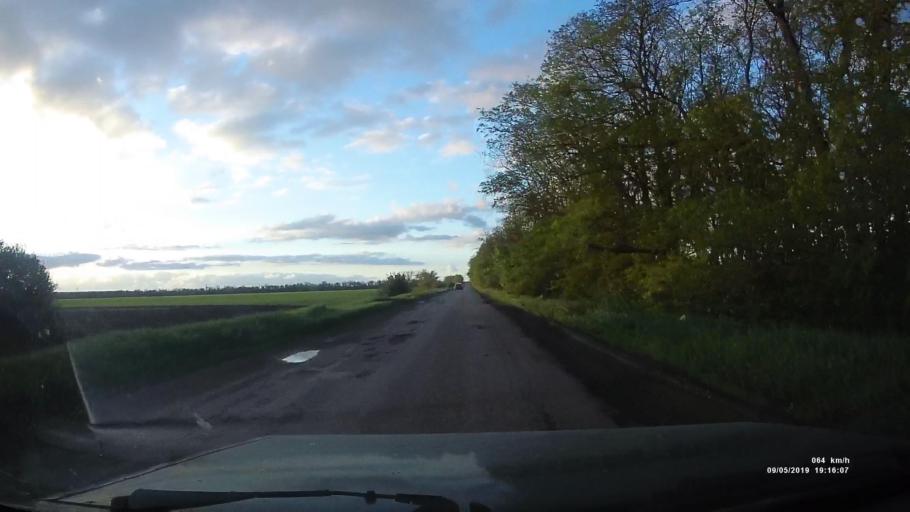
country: RU
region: Krasnodarskiy
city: Kanelovskaya
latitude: 46.7749
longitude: 39.2115
